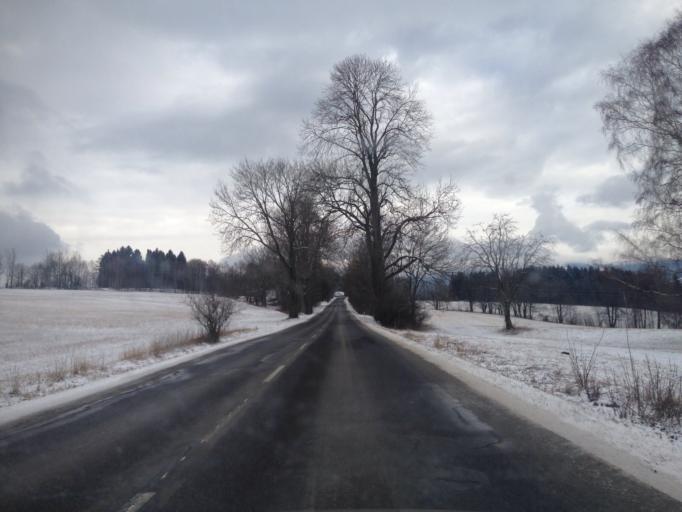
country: CZ
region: Liberecky
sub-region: Okres Semily
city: Vysoke nad Jizerou
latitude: 50.6716
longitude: 15.4087
